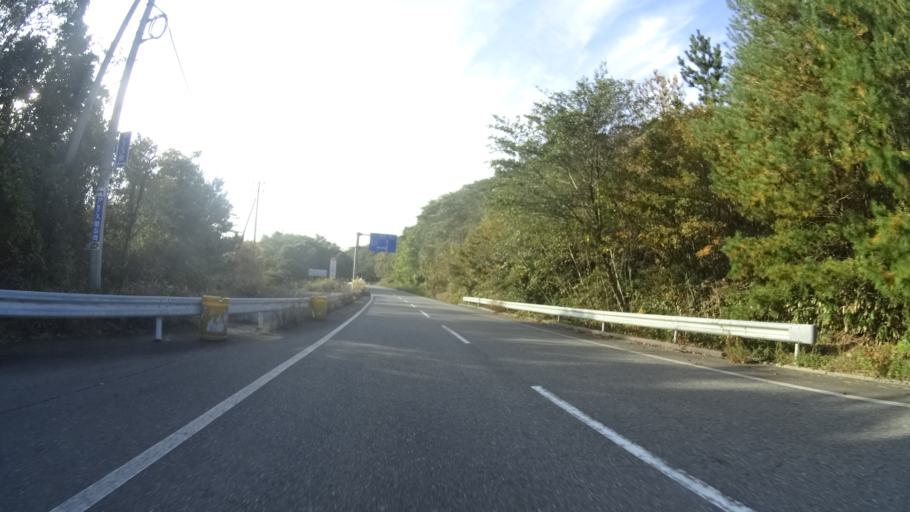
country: JP
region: Ishikawa
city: Hakui
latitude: 37.0707
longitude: 136.7442
